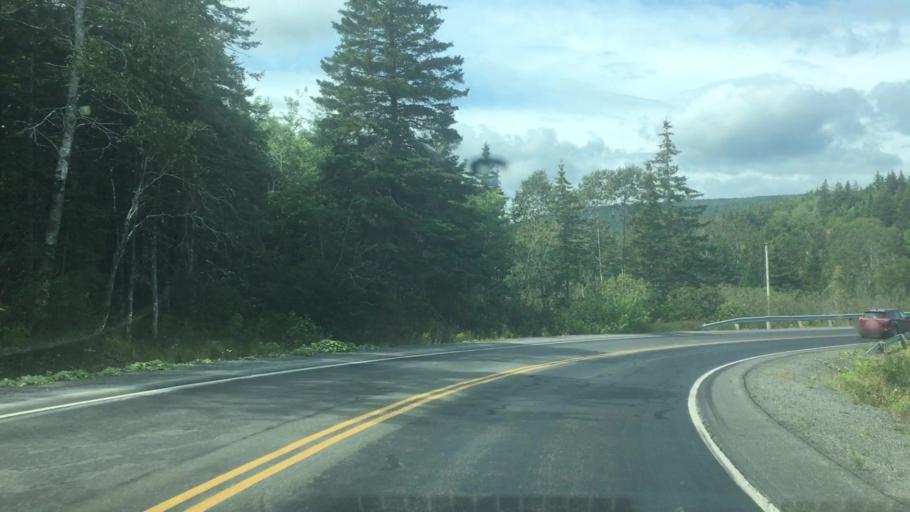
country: CA
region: Nova Scotia
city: Sydney Mines
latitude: 46.2634
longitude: -60.6236
